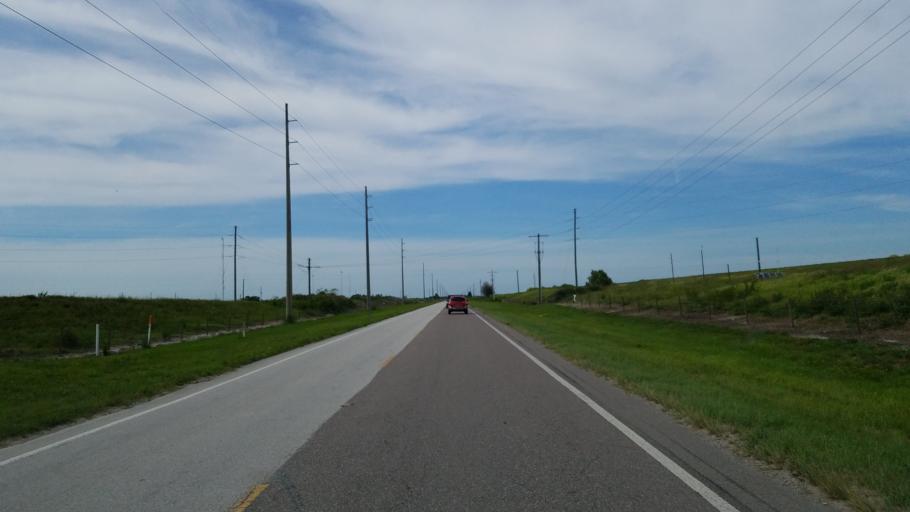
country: US
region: Florida
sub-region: Hillsborough County
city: Balm
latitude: 27.6480
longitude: -82.1463
